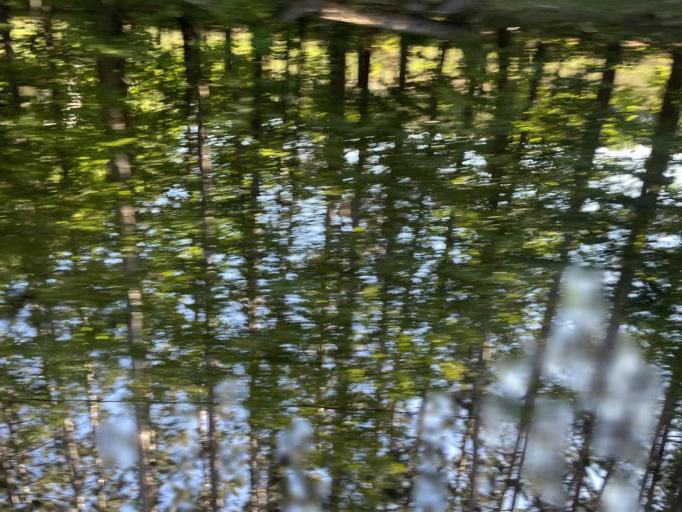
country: US
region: Michigan
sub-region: Benzie County
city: Beulah
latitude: 44.6172
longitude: -86.0466
